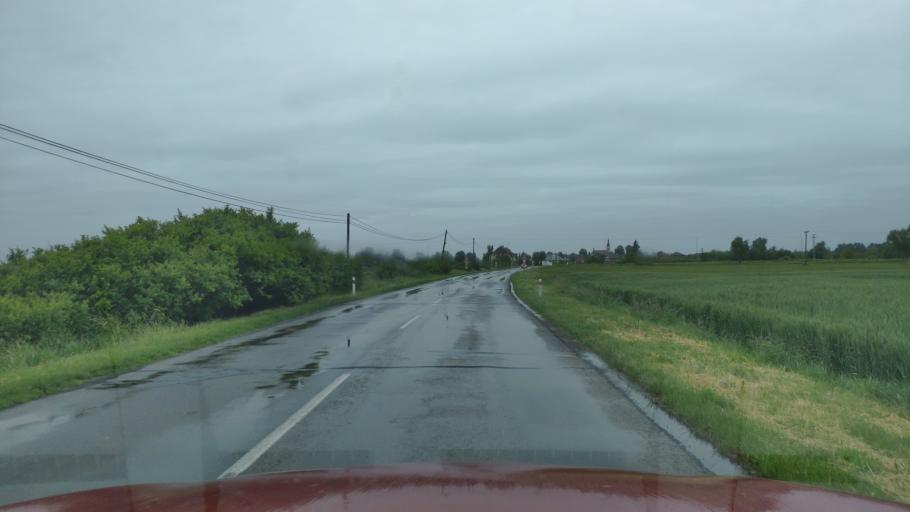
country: SK
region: Kosicky
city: Cierna nad Tisou
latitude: 48.4191
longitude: 22.0265
